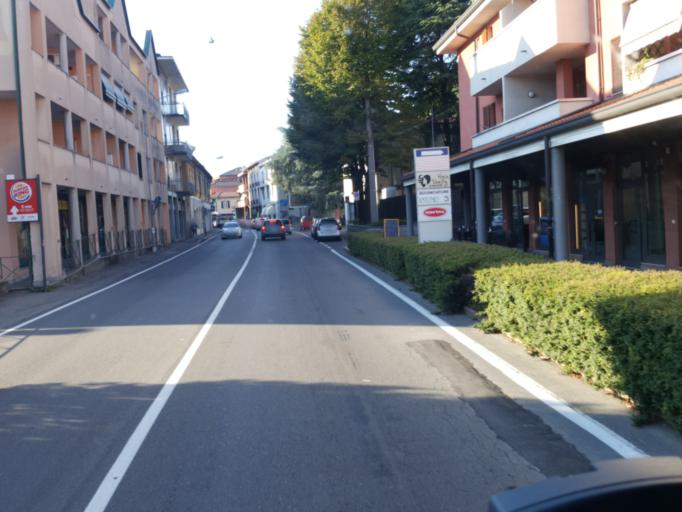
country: IT
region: Lombardy
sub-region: Citta metropolitana di Milano
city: San Vittore Olona
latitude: 45.5844
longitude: 8.9456
